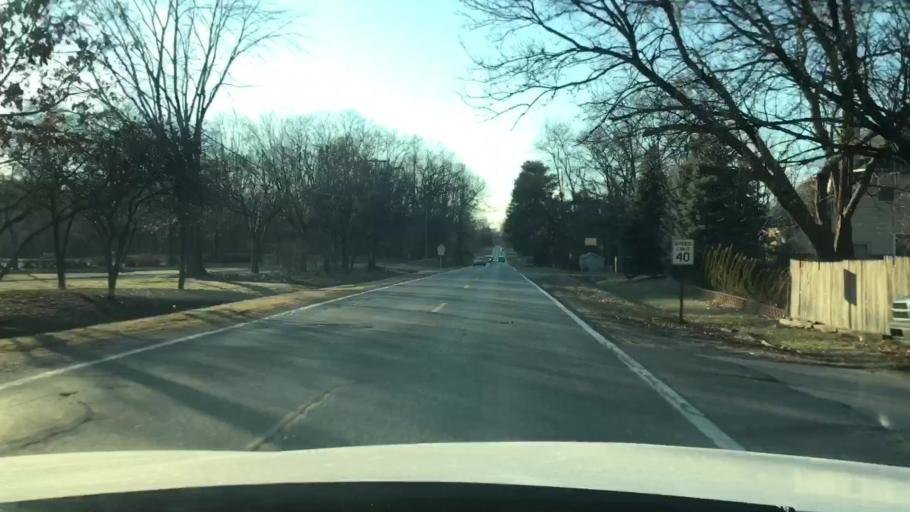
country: US
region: Michigan
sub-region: Oakland County
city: West Bloomfield Township
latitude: 42.5992
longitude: -83.4329
